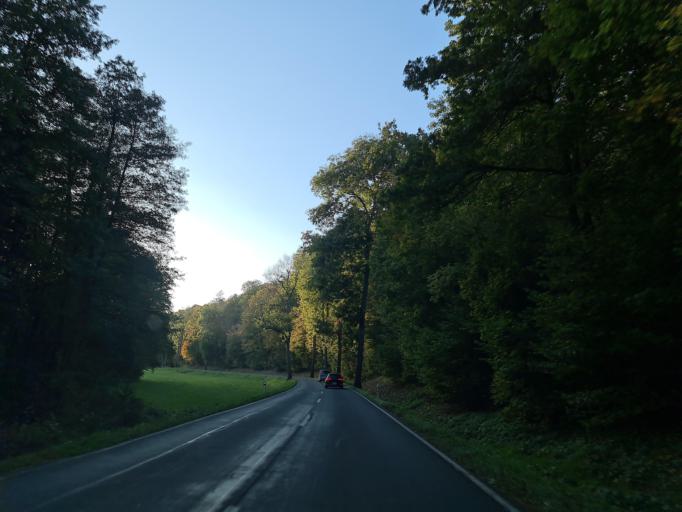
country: DE
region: Saxony
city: Elsterberg
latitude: 50.6064
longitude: 12.1531
